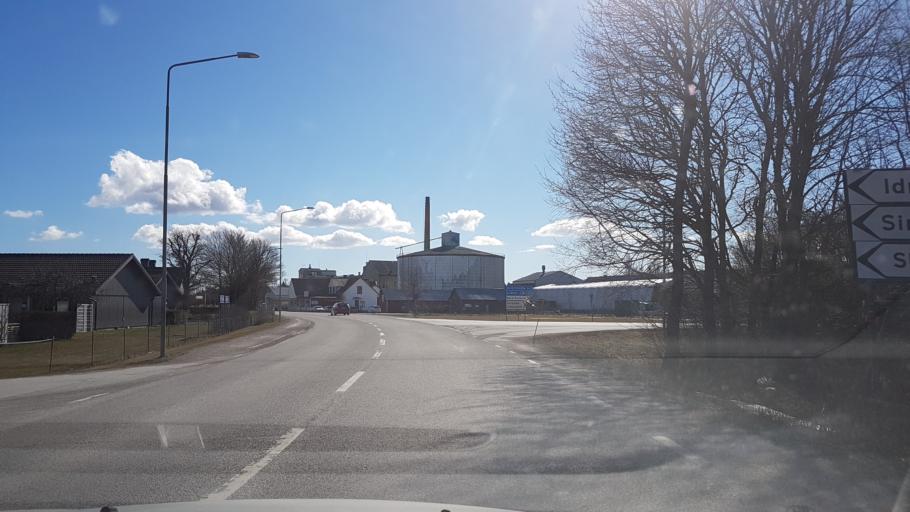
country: SE
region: Gotland
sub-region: Gotland
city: Visby
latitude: 57.5105
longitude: 18.4460
